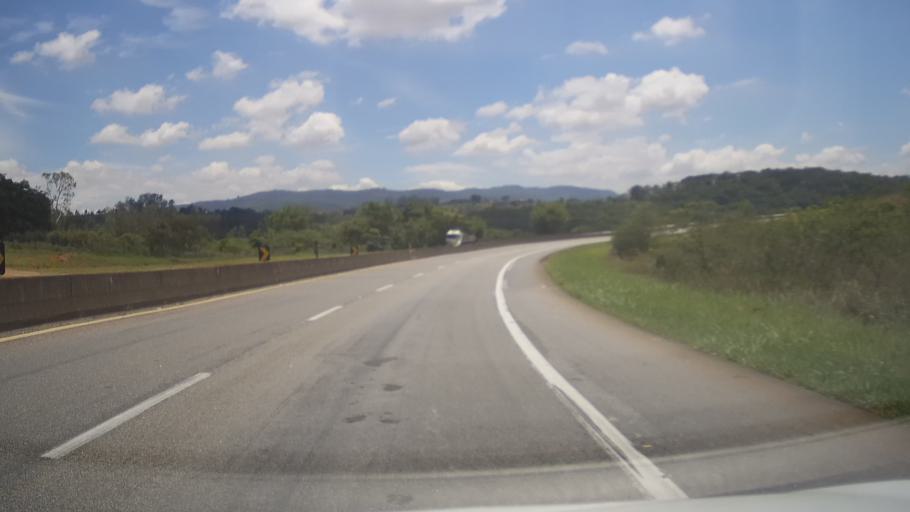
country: BR
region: Minas Gerais
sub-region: Sao Goncalo Do Sapucai
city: Sao Goncalo do Sapucai
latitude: -21.9239
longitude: -45.6123
